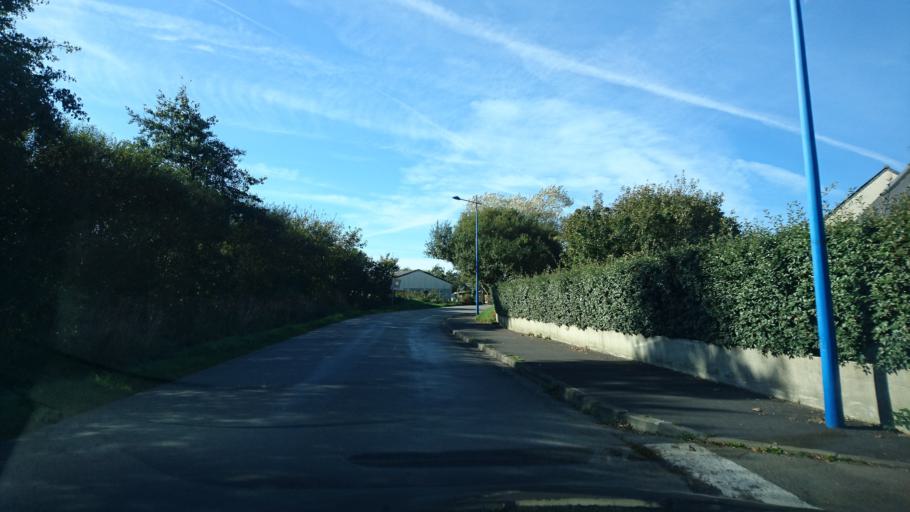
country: FR
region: Brittany
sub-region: Departement du Finistere
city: Plouarzel
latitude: 48.4318
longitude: -4.7317
